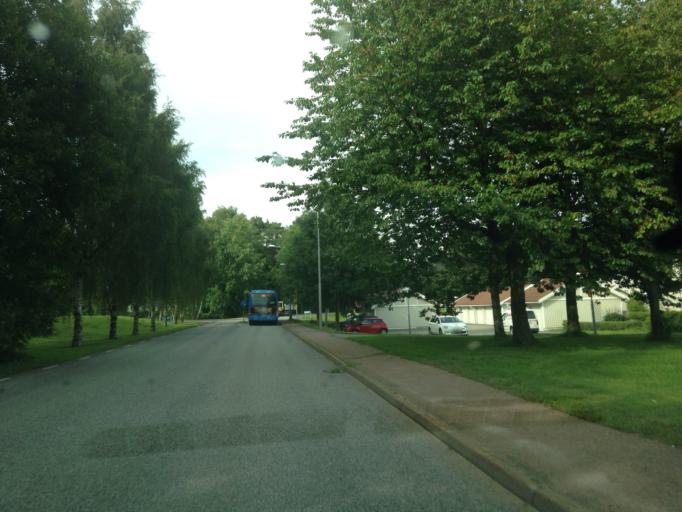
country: SE
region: Vaestra Goetaland
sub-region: Goteborg
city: Goeteborg
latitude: 57.7623
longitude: 11.9692
